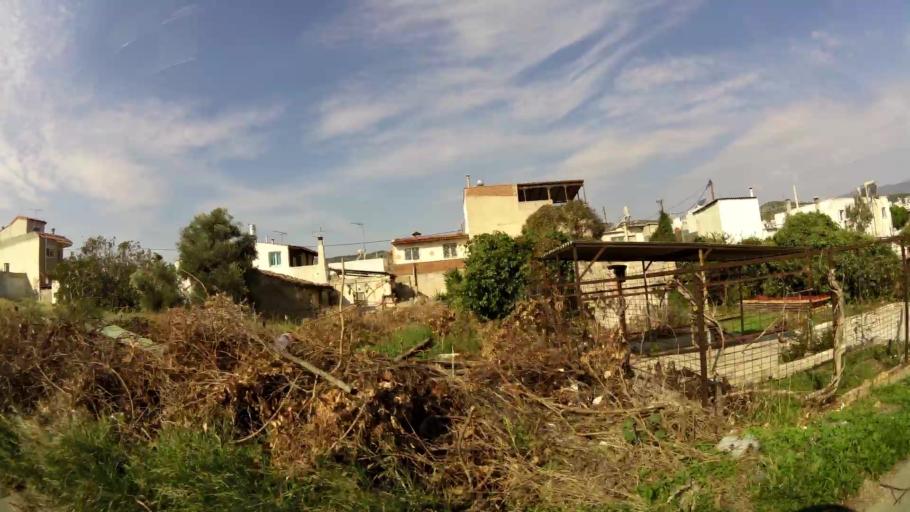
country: GR
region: Attica
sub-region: Nomarchia Athinas
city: Kamateron
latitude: 38.0531
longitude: 23.7107
